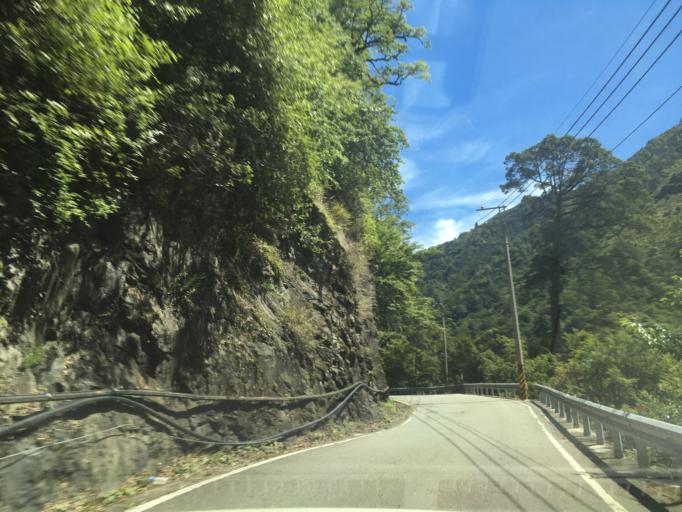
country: TW
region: Taiwan
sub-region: Nantou
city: Puli
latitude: 24.2137
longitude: 121.2657
